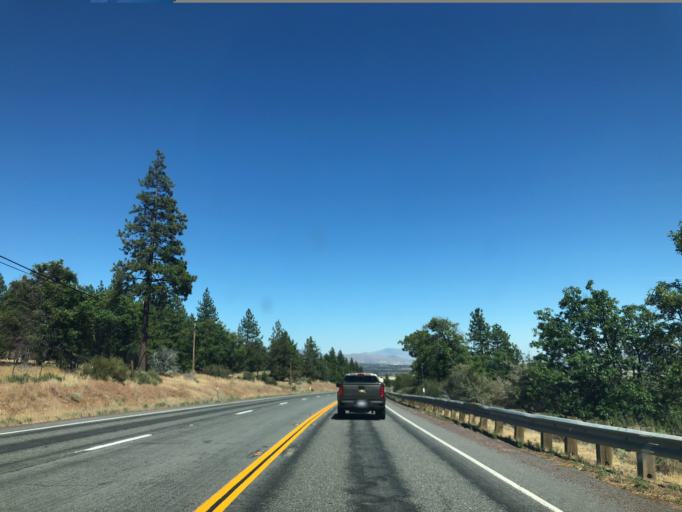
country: US
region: California
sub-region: Lassen County
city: Susanville
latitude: 40.4227
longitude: -120.6915
